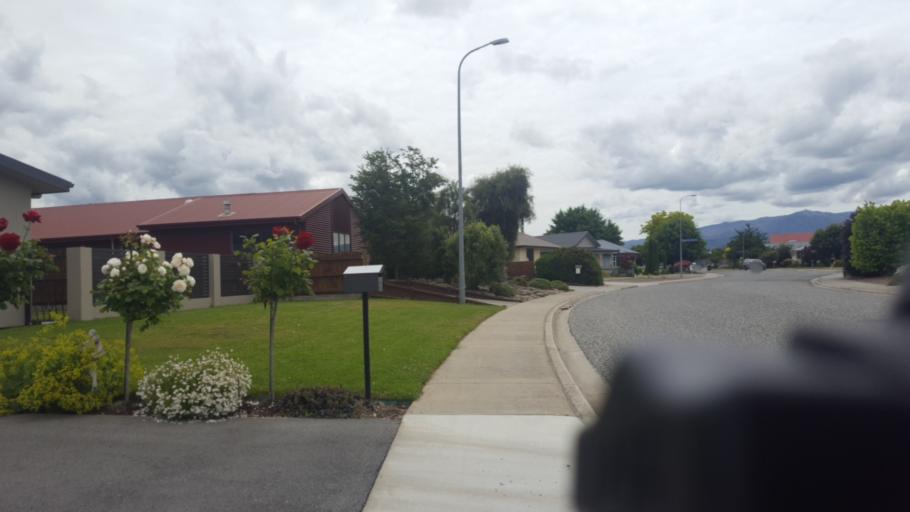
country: NZ
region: Otago
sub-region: Queenstown-Lakes District
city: Wanaka
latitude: -45.2534
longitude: 169.3837
